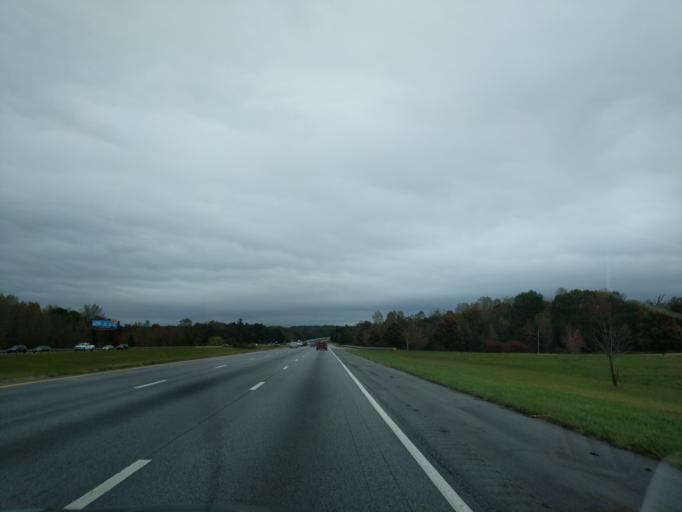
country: US
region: North Carolina
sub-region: Randolph County
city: Trinity
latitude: 35.8735
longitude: -80.0079
